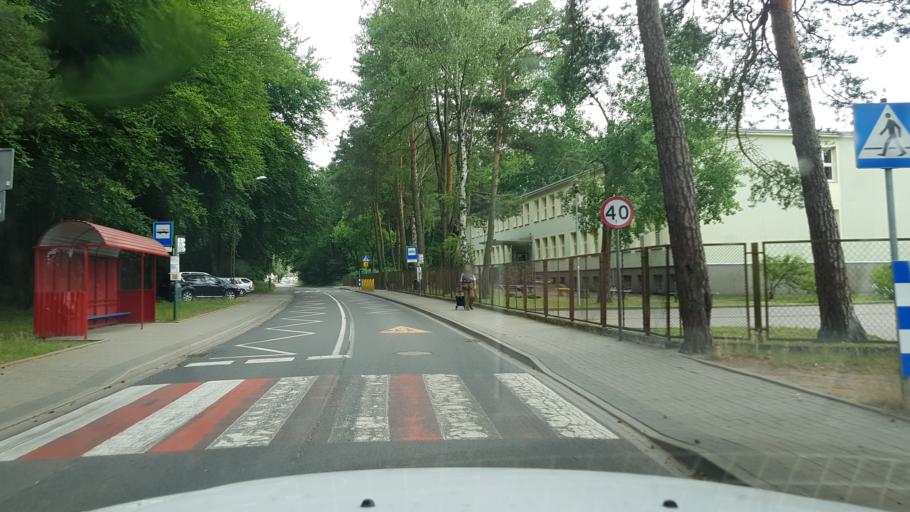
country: PL
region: West Pomeranian Voivodeship
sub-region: Powiat gryfinski
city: Stare Czarnowo
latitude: 53.3862
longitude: 14.7646
